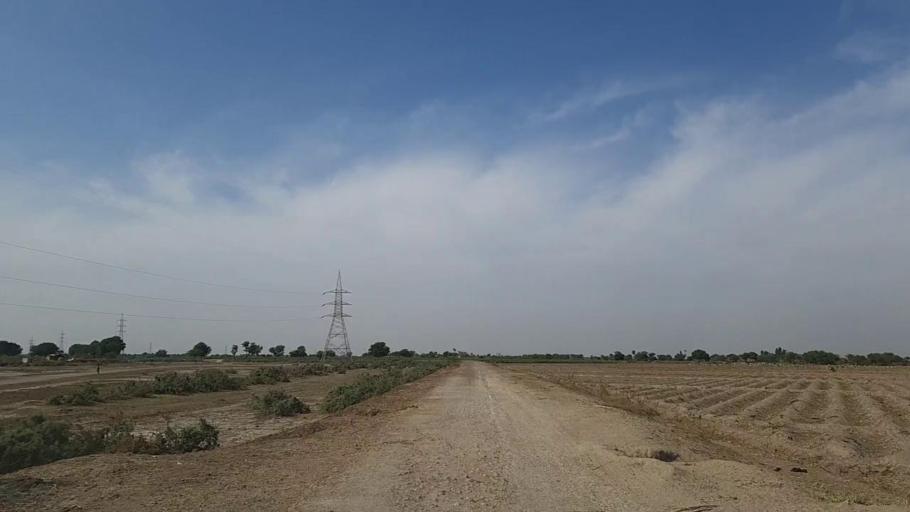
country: PK
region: Sindh
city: Samaro
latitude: 25.2218
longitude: 69.4499
